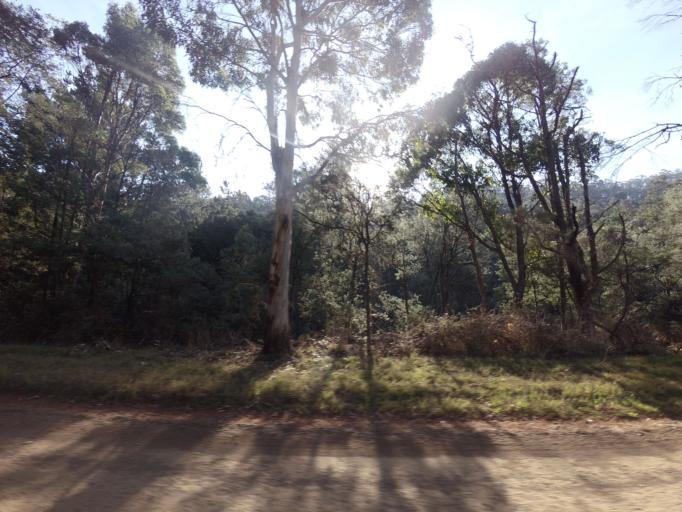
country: AU
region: Tasmania
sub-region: Sorell
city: Sorell
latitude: -42.4876
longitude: 147.4348
